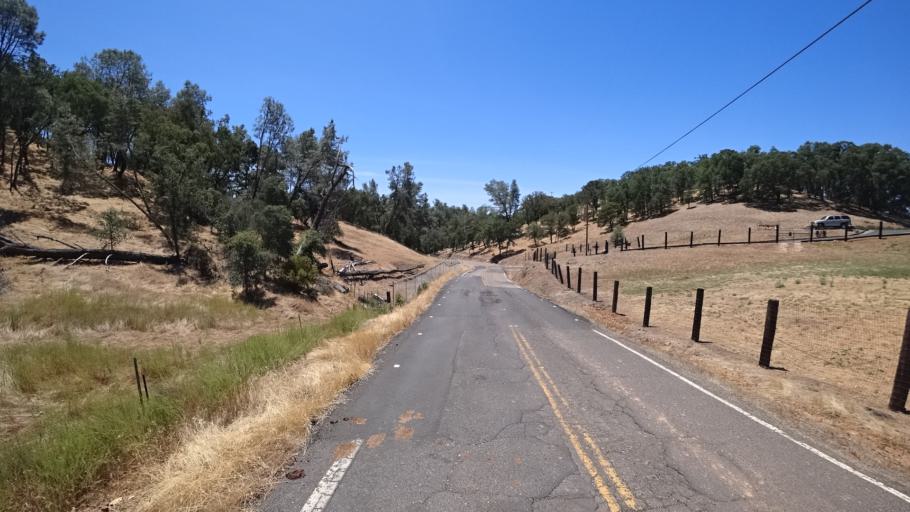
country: US
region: California
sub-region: Calaveras County
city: Valley Springs
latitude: 38.2103
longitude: -120.8626
